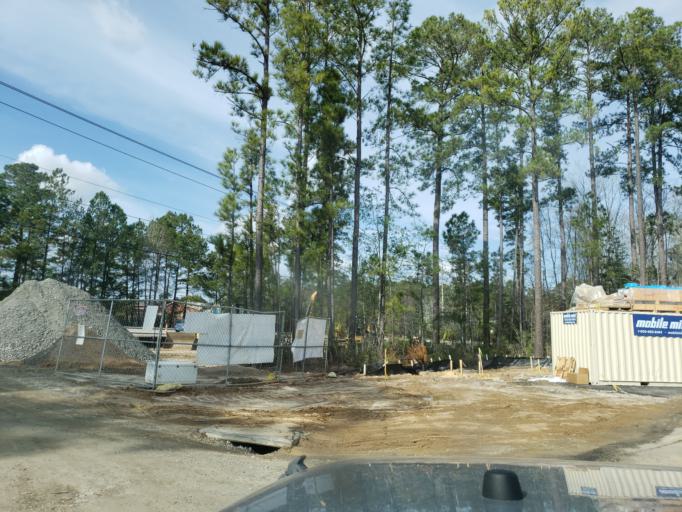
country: US
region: Georgia
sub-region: Chatham County
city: Pooler
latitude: 32.1723
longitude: -81.2330
